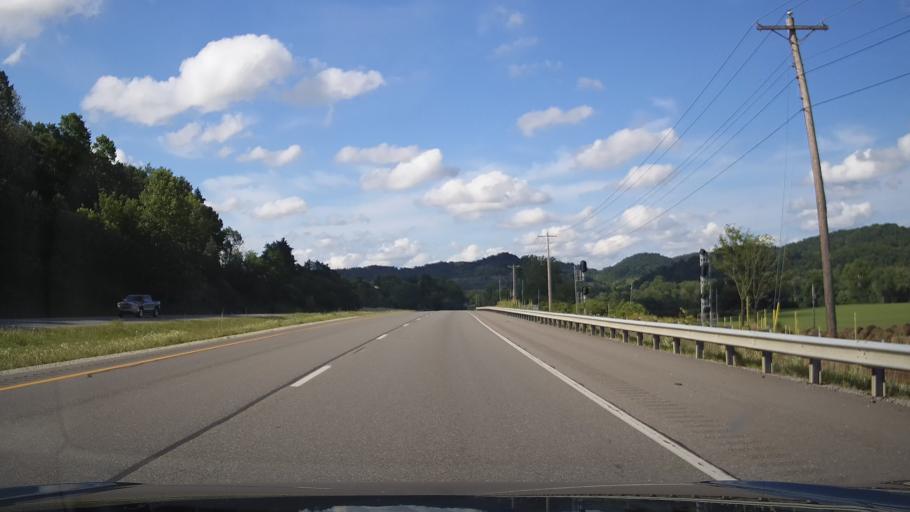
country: US
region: Kentucky
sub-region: Lawrence County
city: Louisa
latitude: 38.2011
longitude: -82.6036
